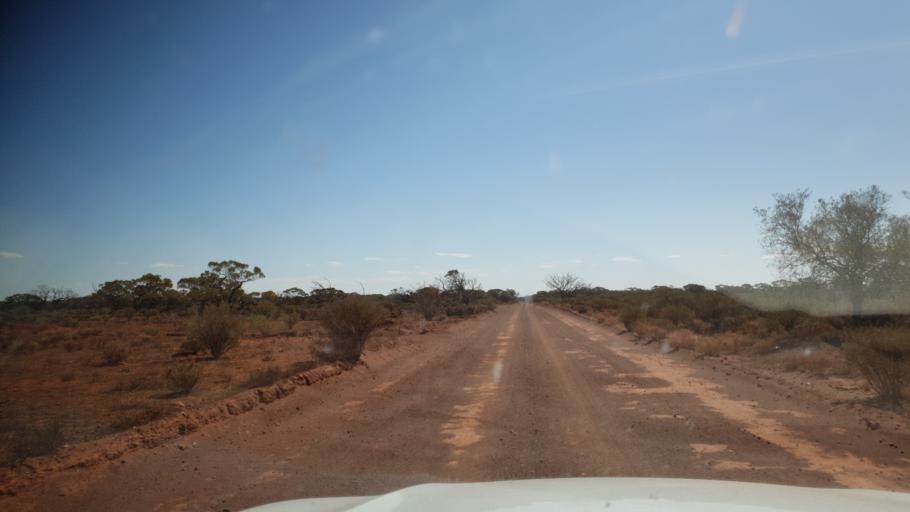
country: AU
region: South Australia
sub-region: Kimba
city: Caralue
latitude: -32.5218
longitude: 136.1402
